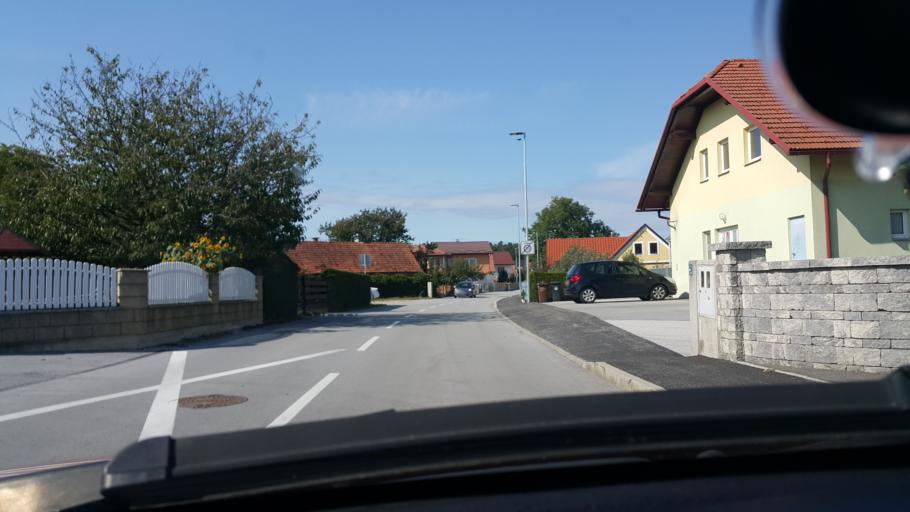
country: SI
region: Miklavz na Dravskem Polju
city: Miklavz na Dravskem Polju
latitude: 46.4820
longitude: 15.7020
